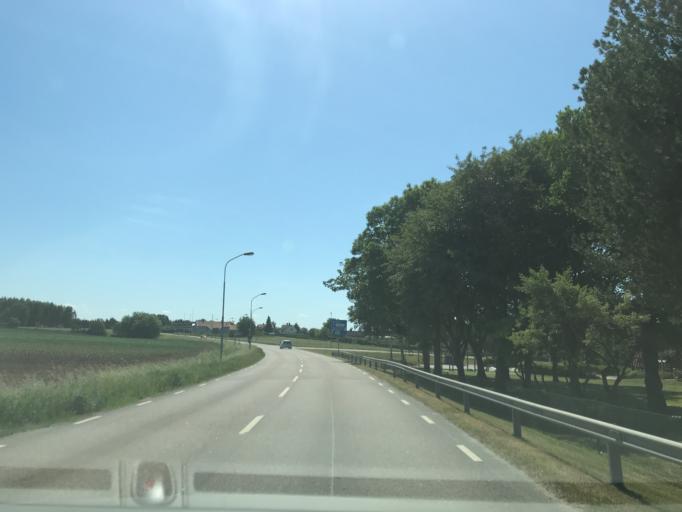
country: SE
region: Vaestra Goetaland
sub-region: Gotene Kommun
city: Kallby
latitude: 58.5090
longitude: 13.3122
